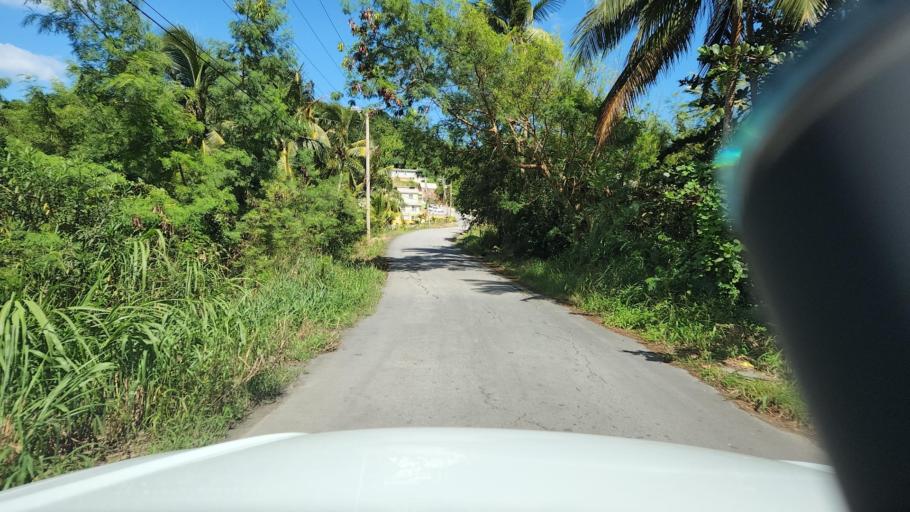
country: BB
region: Saint Joseph
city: Bathsheba
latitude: 13.2129
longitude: -59.5515
